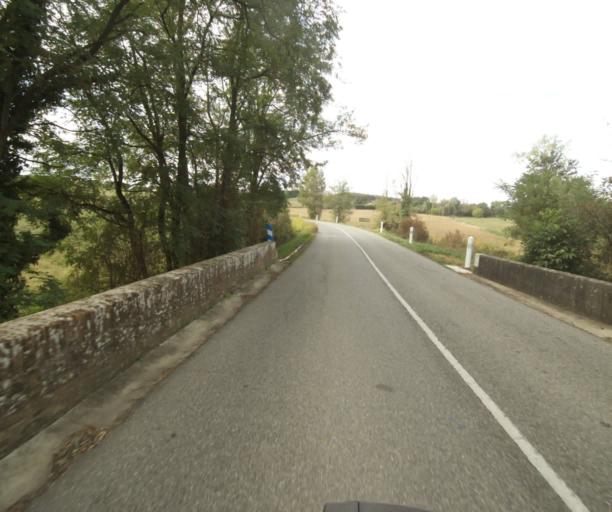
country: FR
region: Midi-Pyrenees
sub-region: Departement du Tarn-et-Garonne
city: Verdun-sur-Garonne
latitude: 43.8542
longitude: 1.1308
